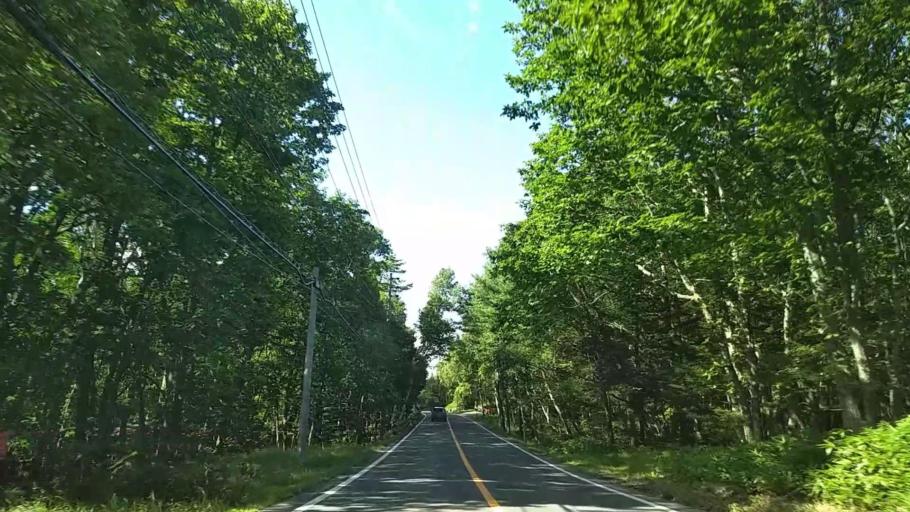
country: JP
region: Nagano
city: Chino
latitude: 36.1044
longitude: 138.2464
